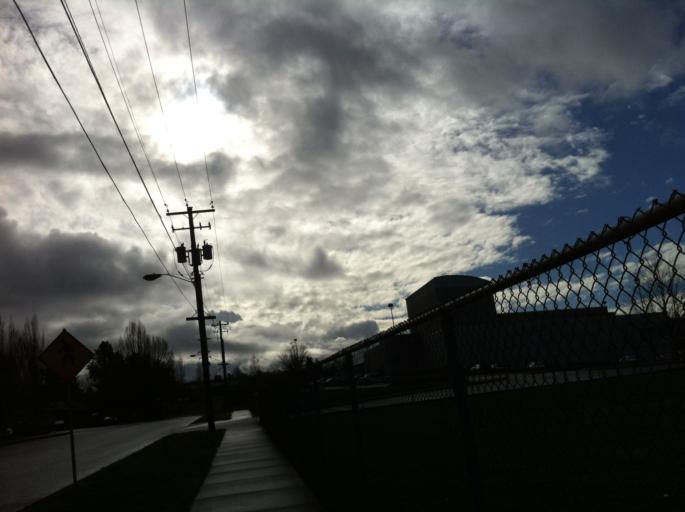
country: US
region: Oregon
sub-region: Multnomah County
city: Lents
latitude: 45.5543
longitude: -122.5383
